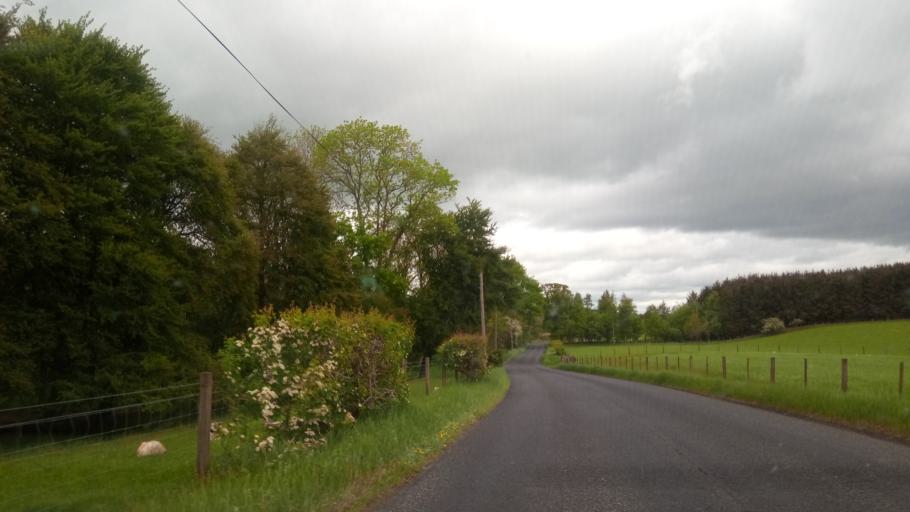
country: GB
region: Scotland
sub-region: The Scottish Borders
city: Hawick
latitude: 55.4672
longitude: -2.7395
